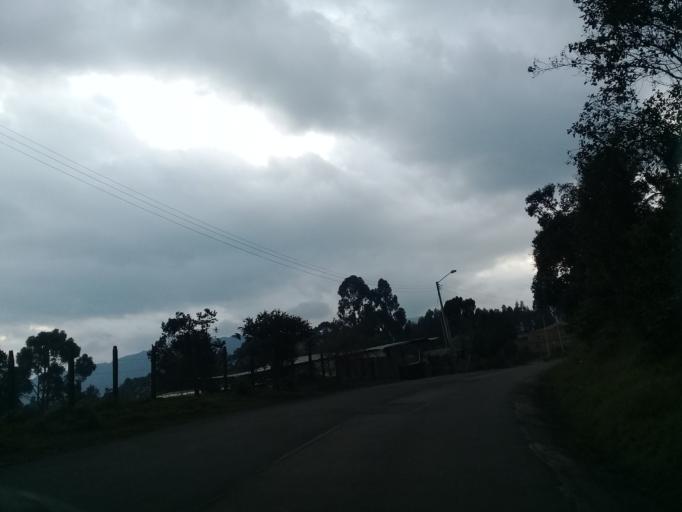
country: CO
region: Cundinamarca
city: Zipaquira
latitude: 5.0408
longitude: -74.0460
